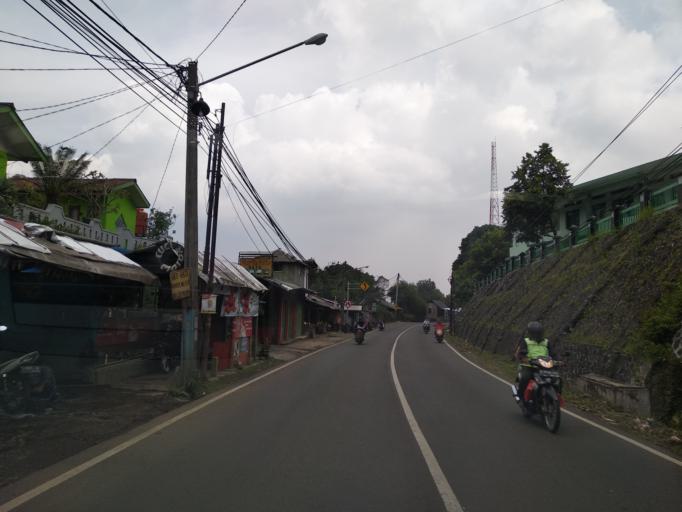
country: ID
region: West Java
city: Lembang
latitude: -6.8248
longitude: 107.6098
